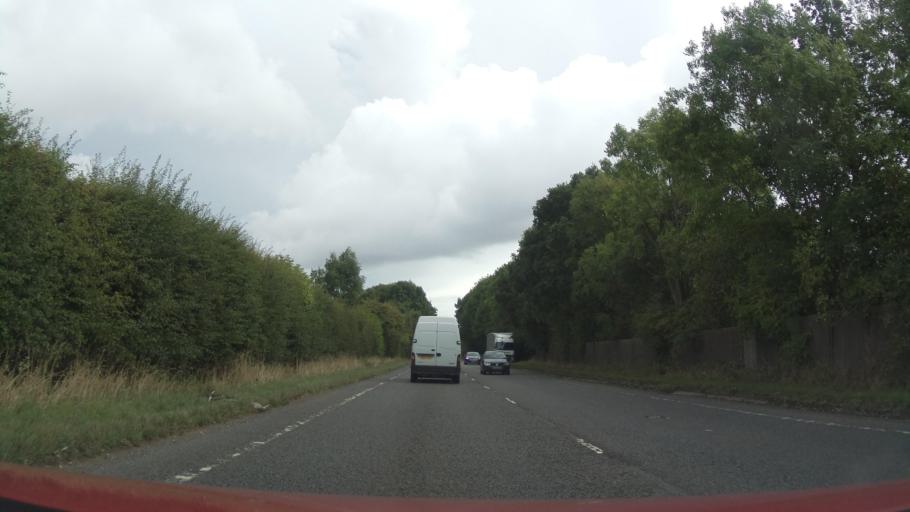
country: GB
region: England
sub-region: Telford and Wrekin
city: Newport
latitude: 52.7753
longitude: -2.3644
